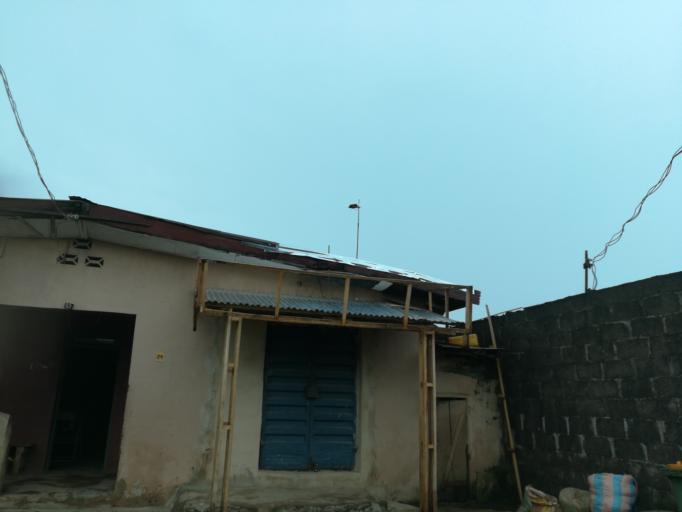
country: NG
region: Lagos
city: Oshodi
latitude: 6.5578
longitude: 3.3426
